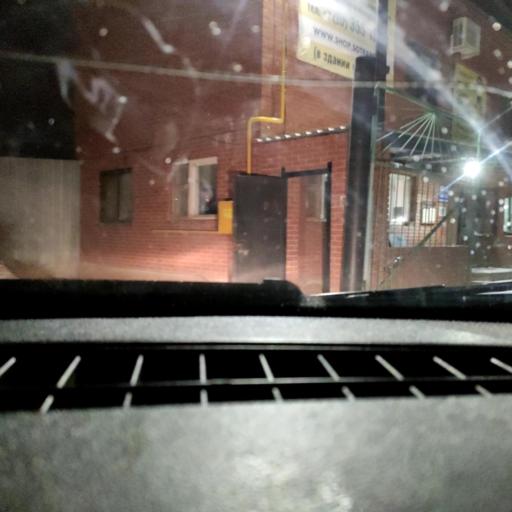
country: RU
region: Bashkortostan
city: Avdon
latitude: 54.6669
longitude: 55.8239
